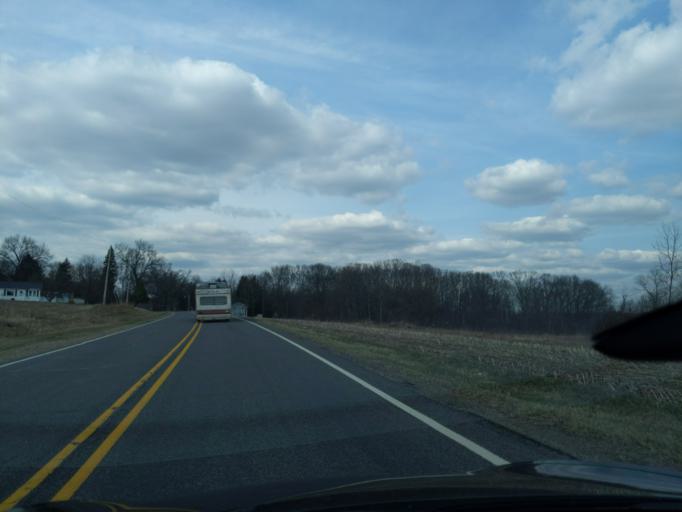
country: US
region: Michigan
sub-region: Ingham County
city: Leslie
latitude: 42.3700
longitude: -84.4170
